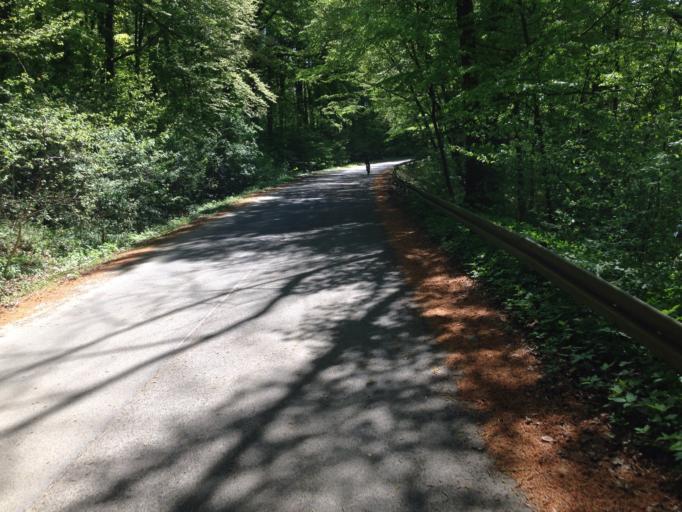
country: DE
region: Hesse
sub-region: Regierungsbezirk Giessen
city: Lich
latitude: 50.5327
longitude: 8.8119
